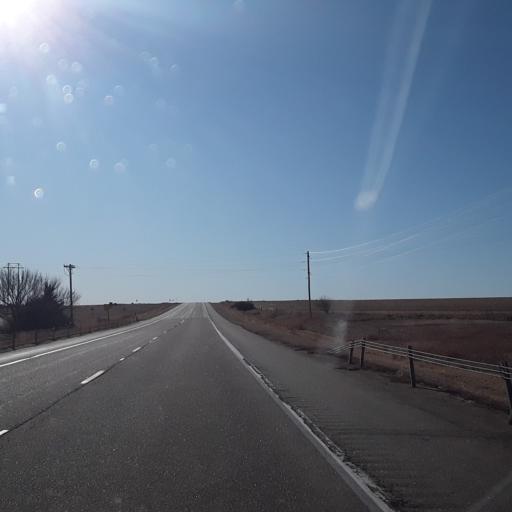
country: US
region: Nebraska
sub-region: Frontier County
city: Stockville
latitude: 40.5515
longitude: -100.6388
